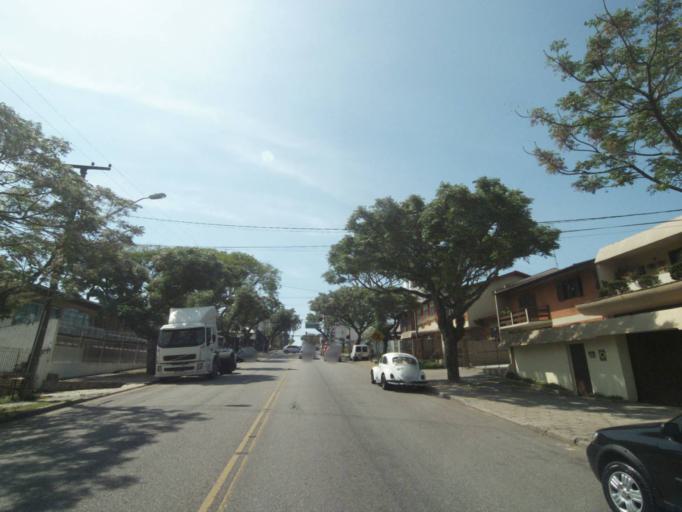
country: BR
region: Parana
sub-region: Curitiba
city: Curitiba
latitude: -25.4764
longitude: -49.2969
